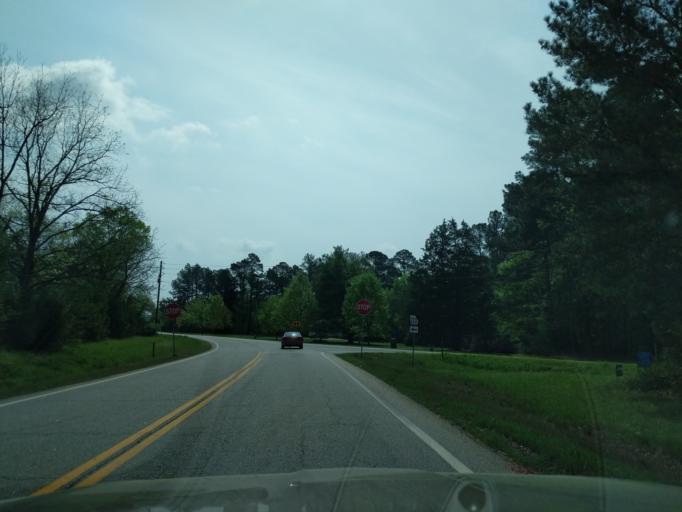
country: US
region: Georgia
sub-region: Lincoln County
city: Lincolnton
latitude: 33.7734
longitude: -82.3753
